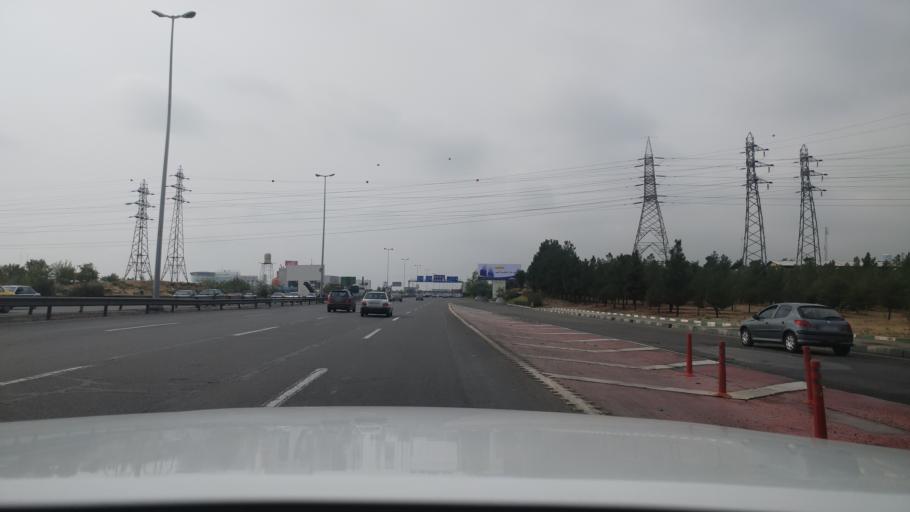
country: IR
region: Tehran
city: Shahr-e Qods
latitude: 35.7149
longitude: 51.2478
